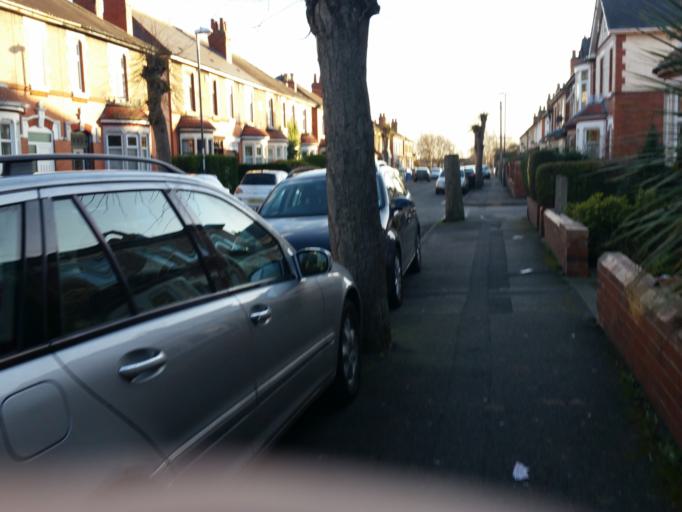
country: GB
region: England
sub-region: Derbyshire
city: Borrowash
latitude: 52.8891
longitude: -1.4192
